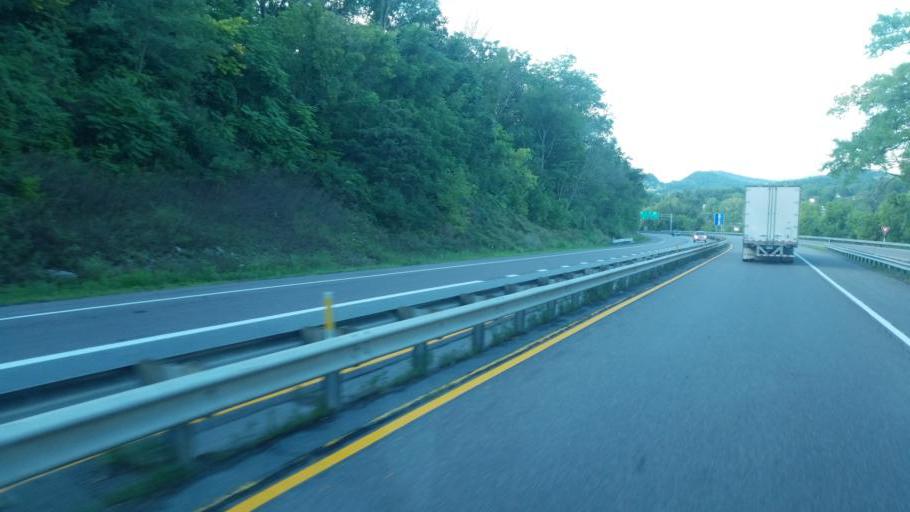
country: US
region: Maryland
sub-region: Washington County
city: Hancock
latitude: 39.7051
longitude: -78.1858
